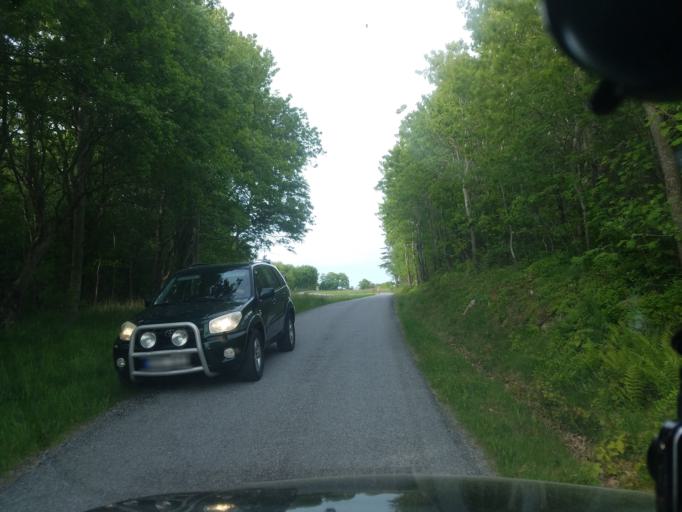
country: SE
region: Vaestra Goetaland
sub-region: Lysekils Kommun
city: Lysekil
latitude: 58.2994
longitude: 11.4493
